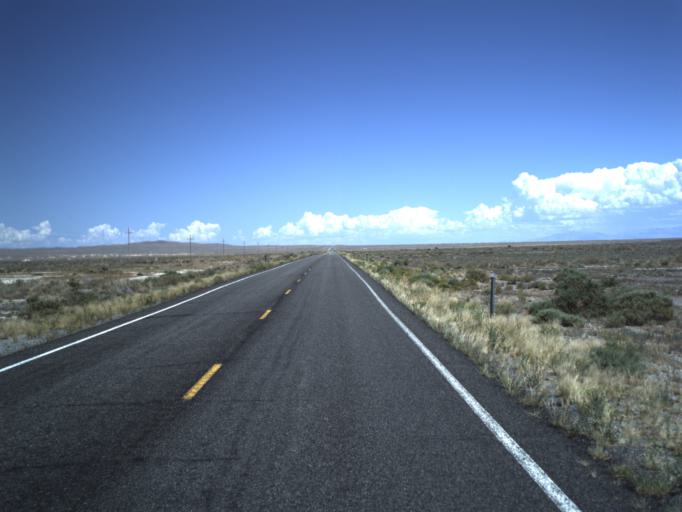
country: US
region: Utah
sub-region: Millard County
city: Delta
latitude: 39.0976
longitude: -113.1591
